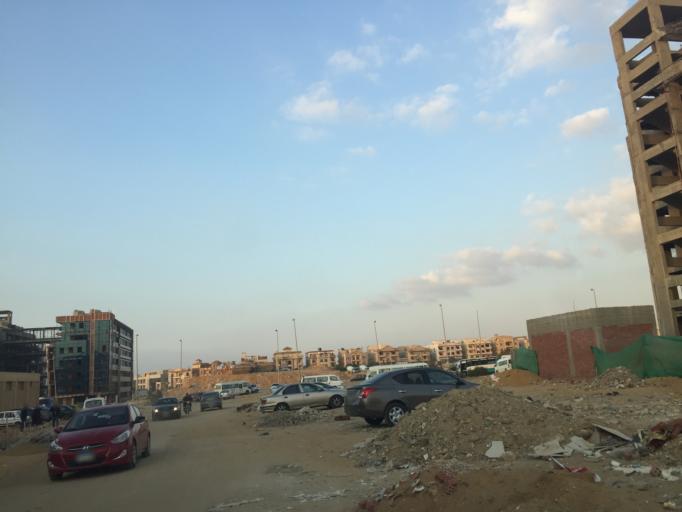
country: EG
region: Muhafazat al Qahirah
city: Cairo
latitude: 30.0187
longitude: 31.4257
